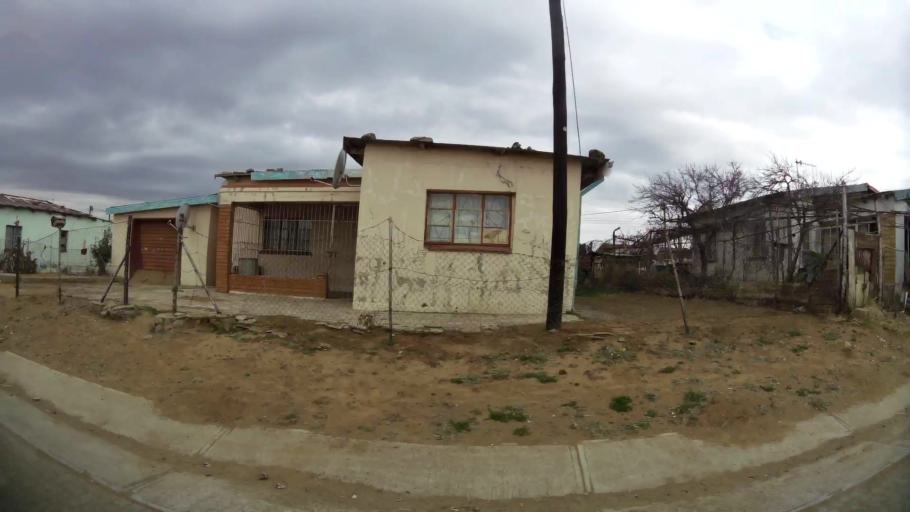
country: ZA
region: Orange Free State
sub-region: Fezile Dabi District Municipality
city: Kroonstad
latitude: -27.6472
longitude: 27.2058
